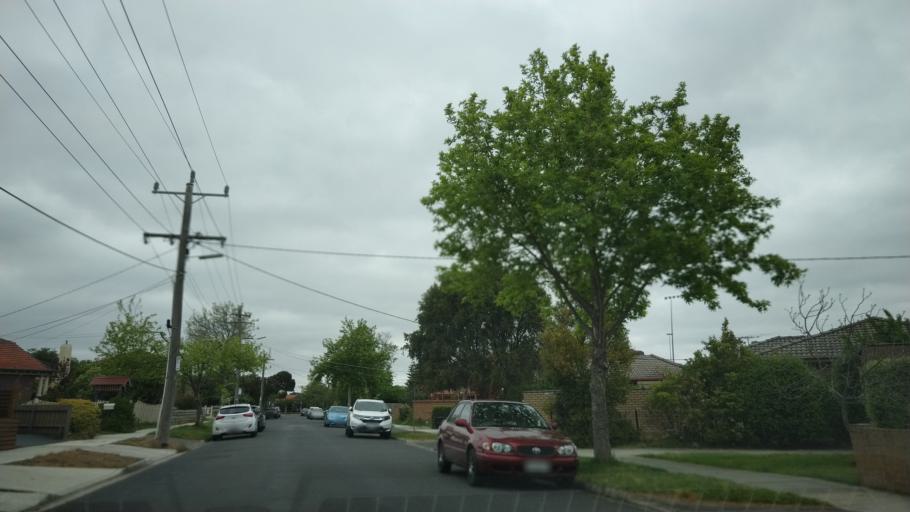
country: AU
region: Victoria
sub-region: Glen Eira
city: Murrumbeena
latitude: -37.8950
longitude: 145.0732
